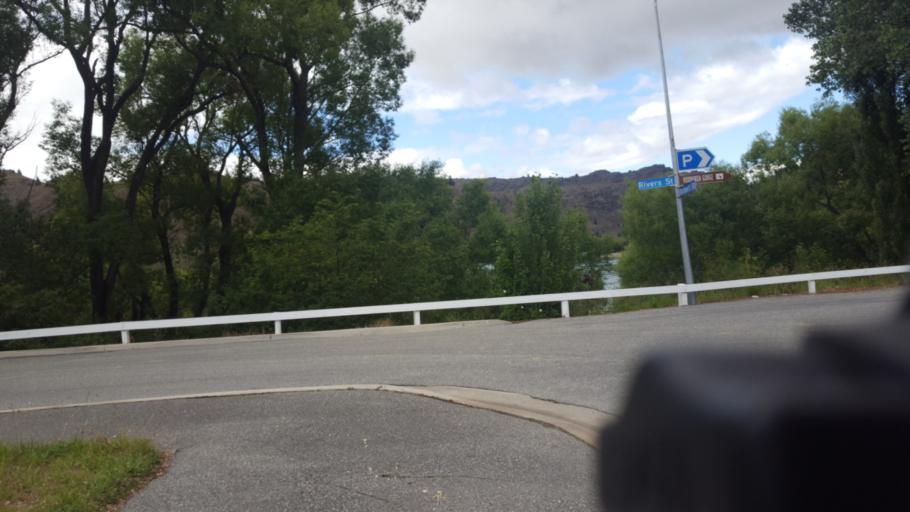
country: NZ
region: Otago
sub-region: Queenstown-Lakes District
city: Wanaka
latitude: -45.2586
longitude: 169.3932
